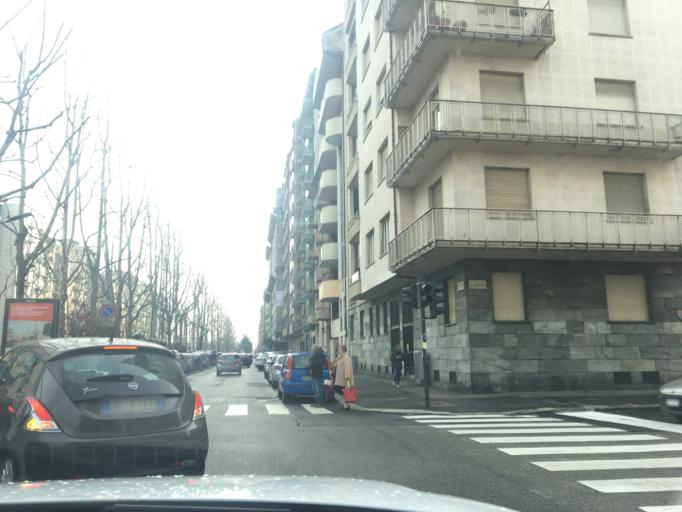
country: IT
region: Piedmont
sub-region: Provincia di Torino
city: Lesna
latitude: 45.0379
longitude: 7.6450
